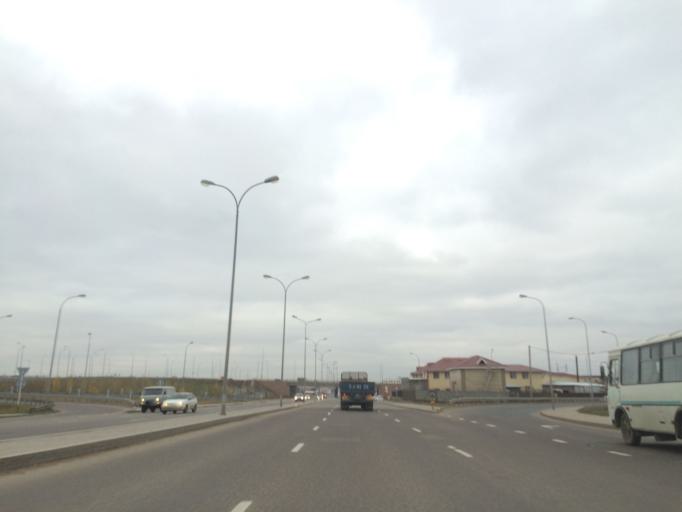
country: KZ
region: Astana Qalasy
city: Astana
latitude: 51.1721
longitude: 71.4874
